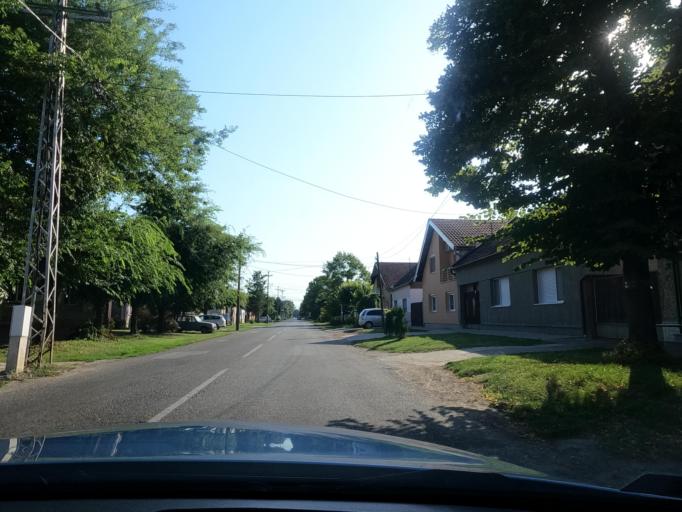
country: RS
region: Autonomna Pokrajina Vojvodina
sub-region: Juznobacki Okrug
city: Becej
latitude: 45.6093
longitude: 20.0405
